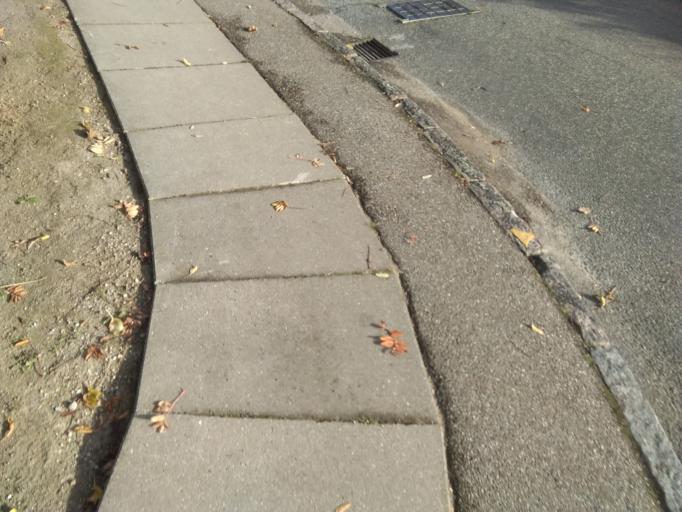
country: DK
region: Capital Region
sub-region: Kobenhavn
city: Vanlose
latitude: 55.6992
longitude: 12.4939
